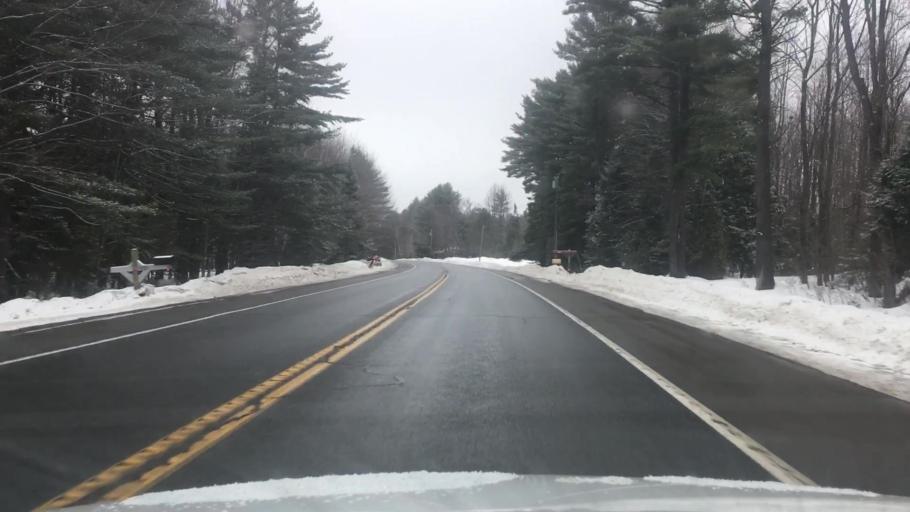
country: US
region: Maine
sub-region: Franklin County
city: New Sharon
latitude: 44.6571
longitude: -69.9567
